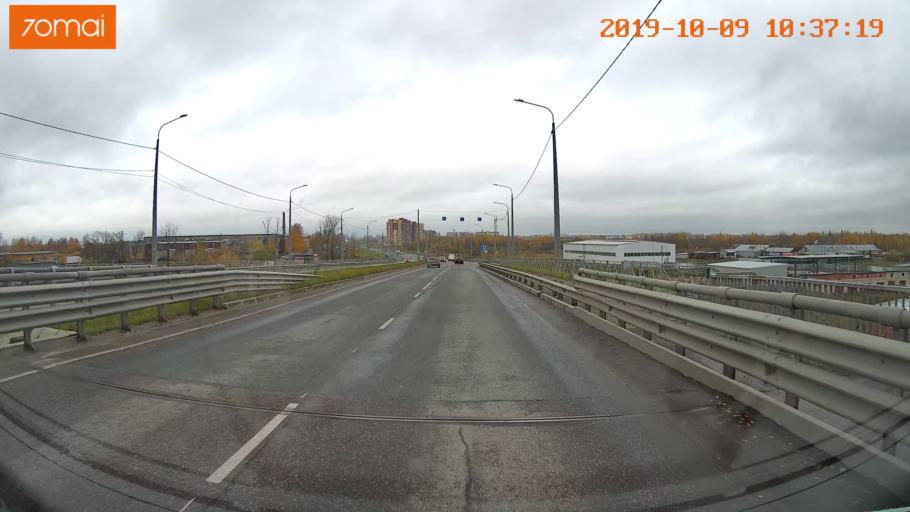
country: RU
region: Vologda
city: Vologda
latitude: 59.2343
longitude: 39.8649
